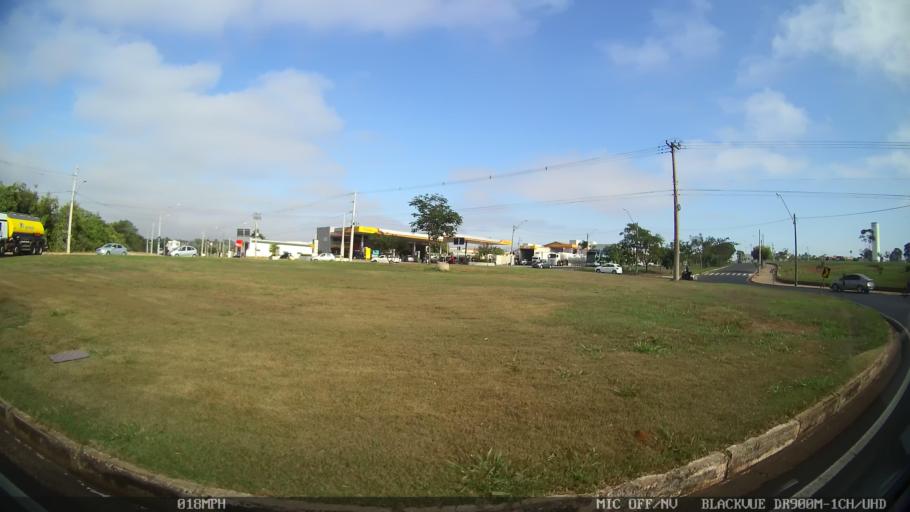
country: BR
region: Sao Paulo
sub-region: Sao Jose Do Rio Preto
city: Sao Jose do Rio Preto
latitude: -20.8052
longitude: -49.4253
